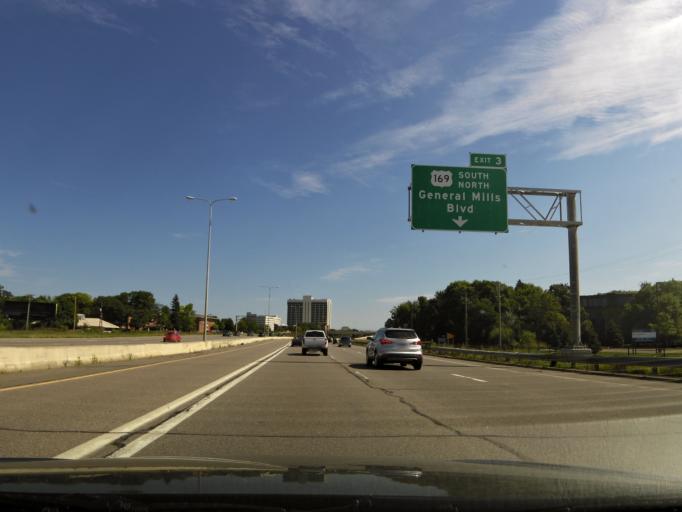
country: US
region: Minnesota
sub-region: Hennepin County
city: Minnetonka Mills
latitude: 44.9723
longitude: -93.4148
